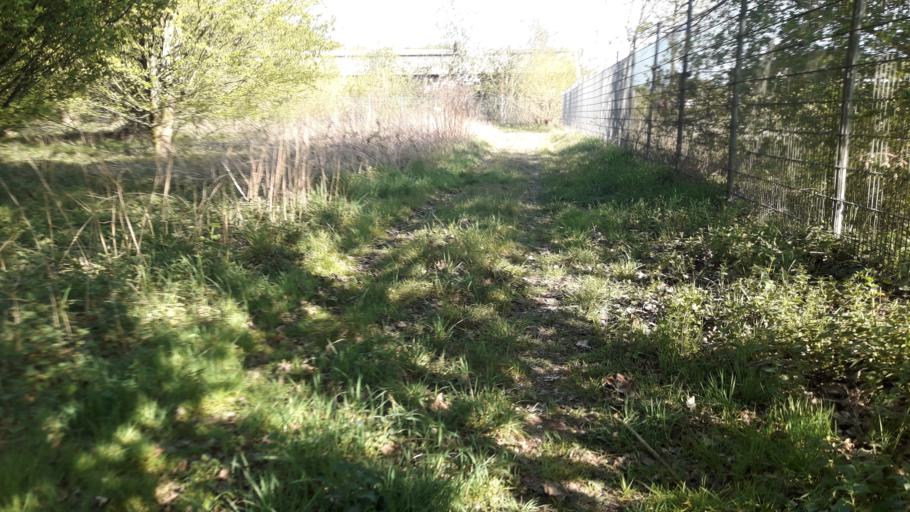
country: DE
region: North Rhine-Westphalia
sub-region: Regierungsbezirk Detmold
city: Salzkotten
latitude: 51.7050
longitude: 8.6619
